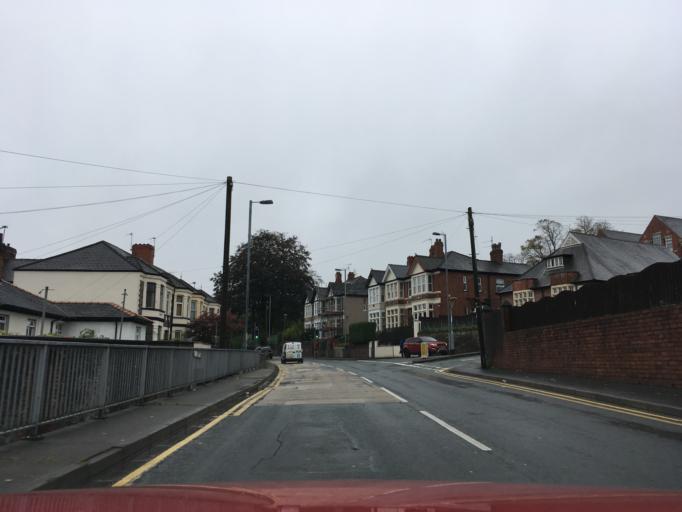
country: GB
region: Wales
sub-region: Newport
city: Newport
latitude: 51.5928
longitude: -2.9998
